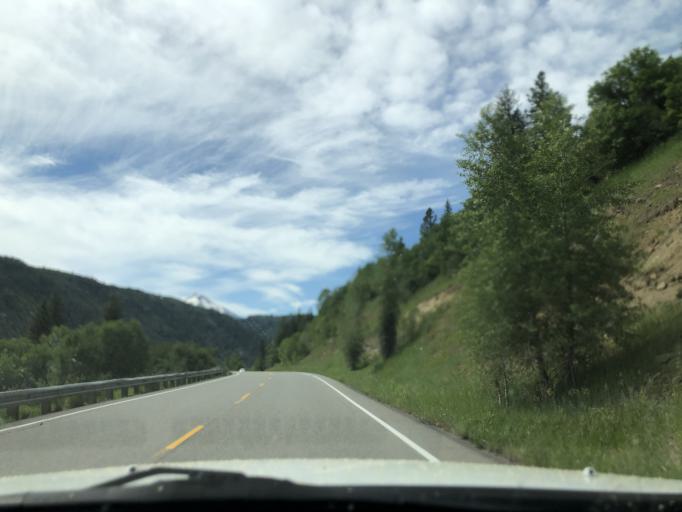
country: US
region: Colorado
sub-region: Delta County
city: Paonia
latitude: 38.9750
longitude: -107.3424
